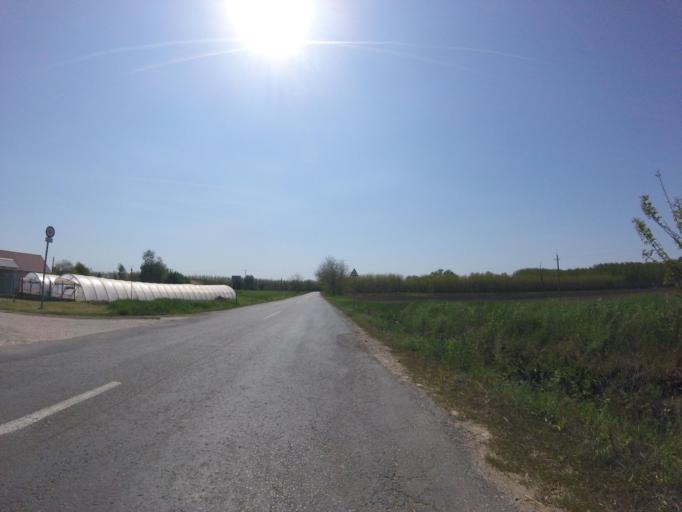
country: HU
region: Pest
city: Ujhartyan
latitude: 47.2386
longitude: 19.4426
